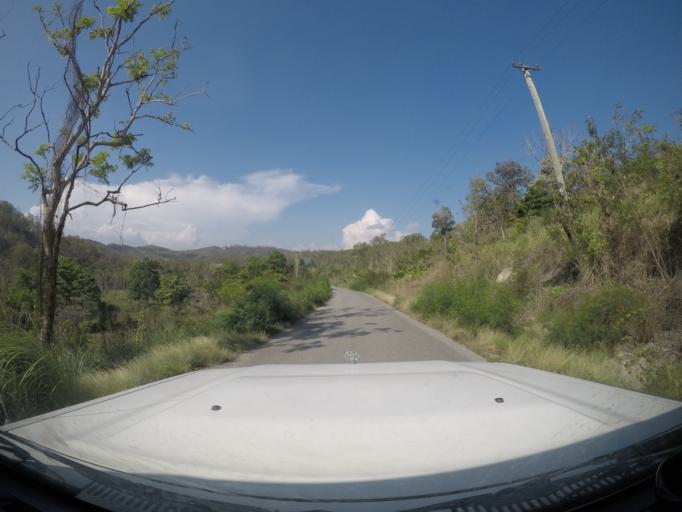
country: PG
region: Central Province
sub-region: Rigo
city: Kwikila
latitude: -9.8585
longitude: 147.5645
